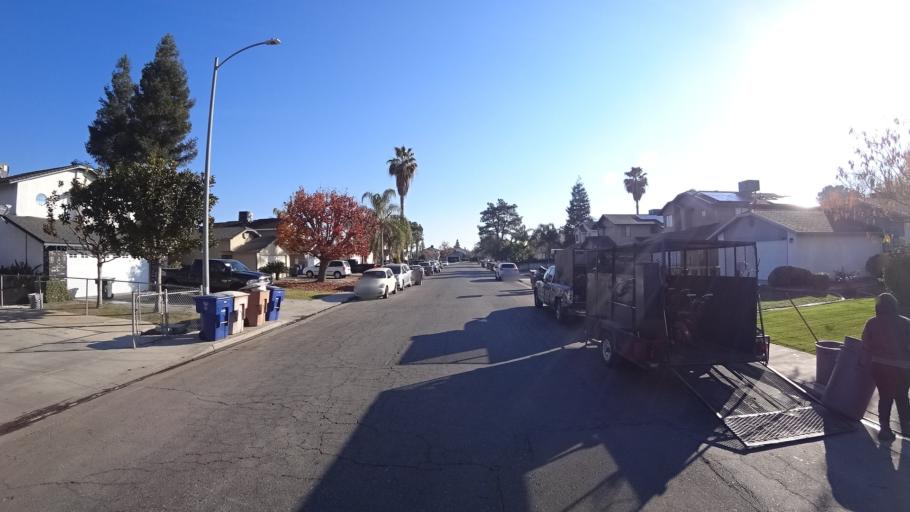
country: US
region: California
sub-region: Kern County
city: Greenfield
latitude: 35.2973
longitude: -119.0145
